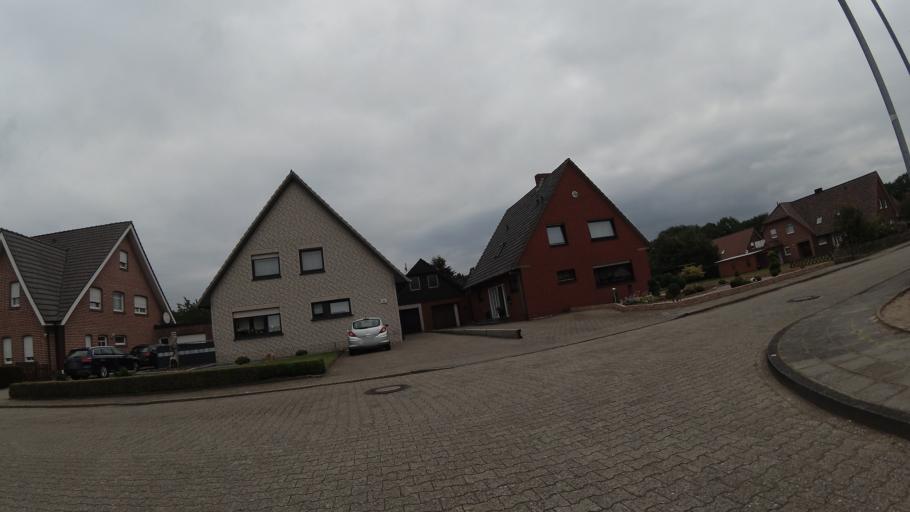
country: DE
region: Lower Saxony
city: Fresenburg
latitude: 52.8815
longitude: 7.3116
